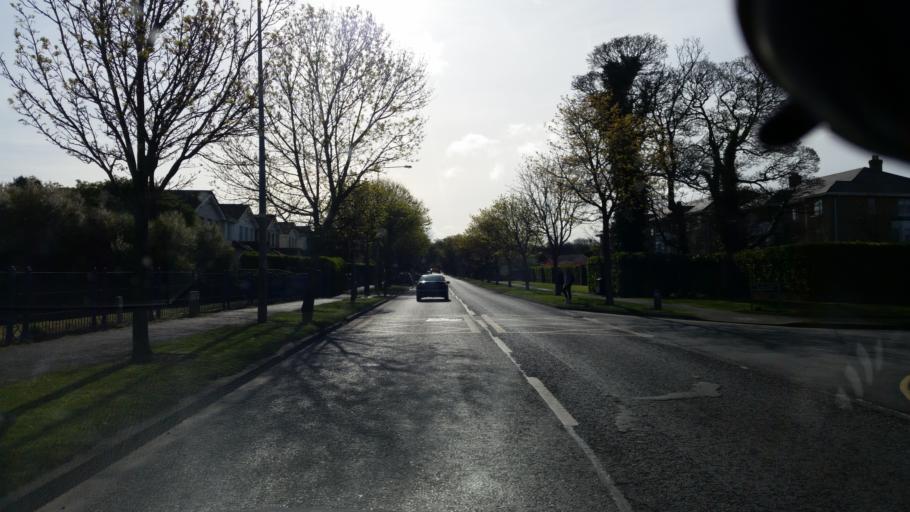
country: IE
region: Leinster
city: Kinsealy-Drinan
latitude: 53.4483
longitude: -6.1799
